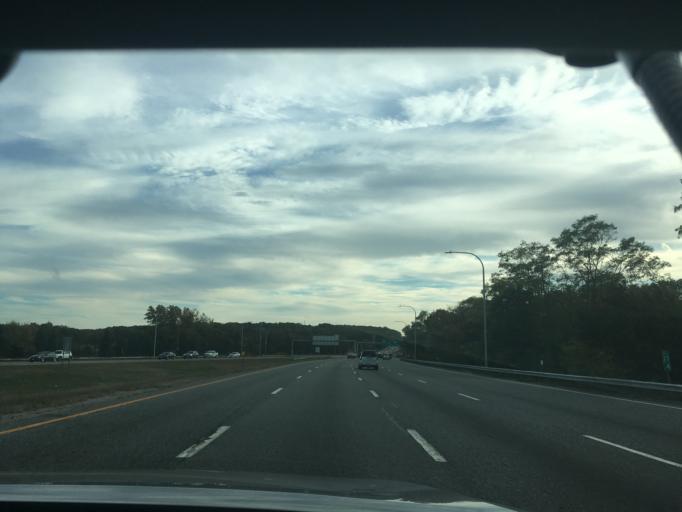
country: US
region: Rhode Island
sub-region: Kent County
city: East Greenwich
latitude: 41.7045
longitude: -71.4737
